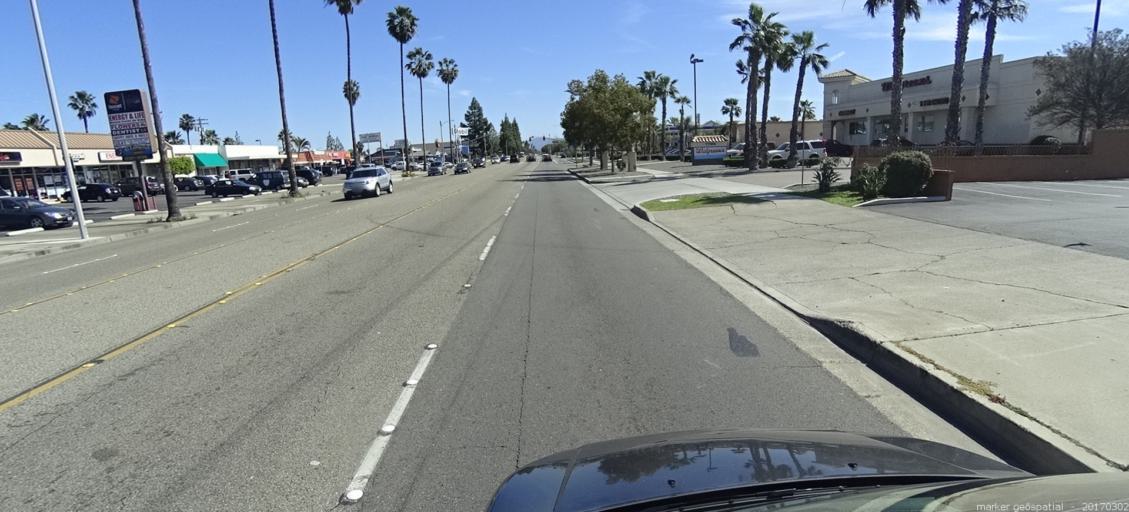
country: US
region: California
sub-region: Orange County
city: Fullerton
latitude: 33.8470
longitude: -117.9435
